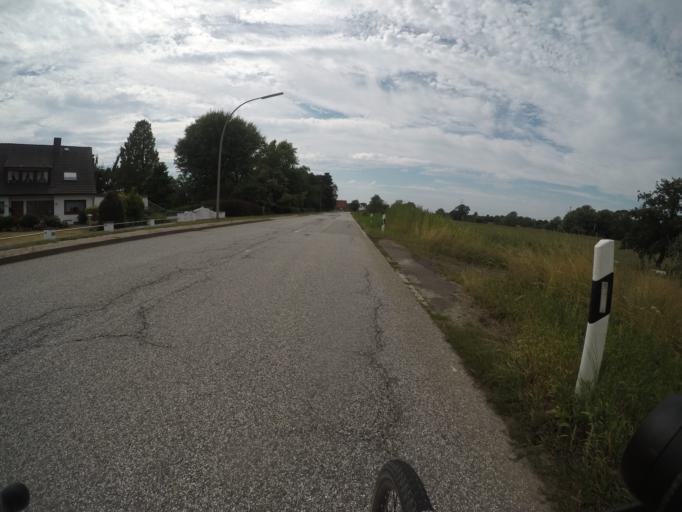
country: DE
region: Hamburg
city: Bergedorf
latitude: 53.4690
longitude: 10.1571
